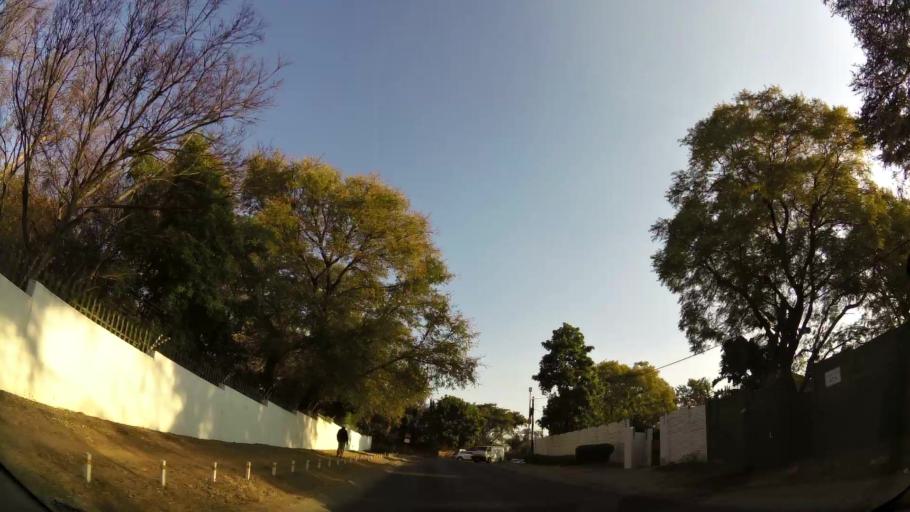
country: ZA
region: Gauteng
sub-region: City of Johannesburg Metropolitan Municipality
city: Johannesburg
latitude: -26.0717
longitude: 27.9994
